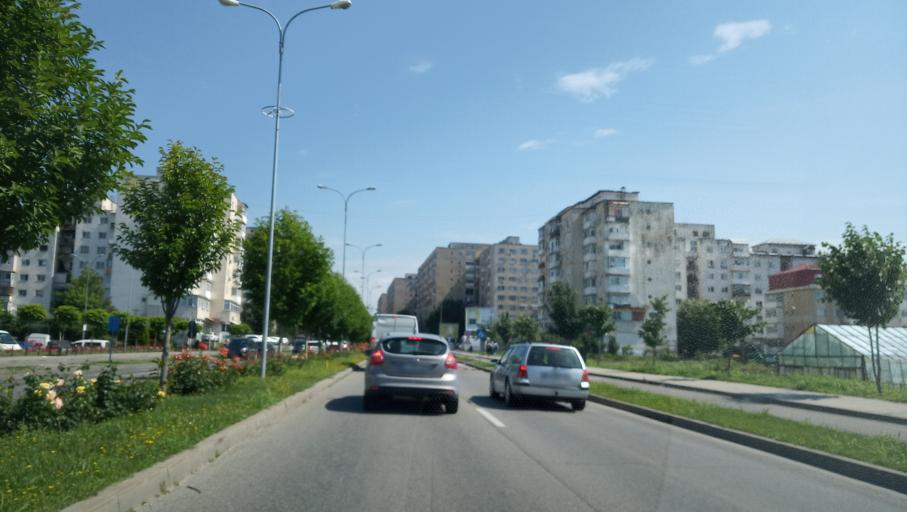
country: RO
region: Valcea
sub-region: Municipiul Ramnicu Valcea
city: Ramnicu Valcea
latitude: 45.0907
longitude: 24.3710
